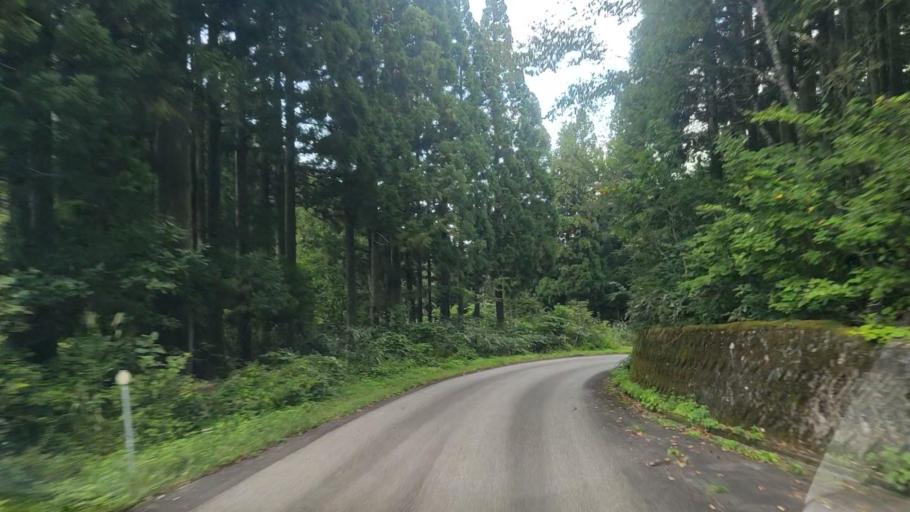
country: JP
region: Toyama
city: Yatsuomachi-higashikumisaka
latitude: 36.4181
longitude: 137.0814
